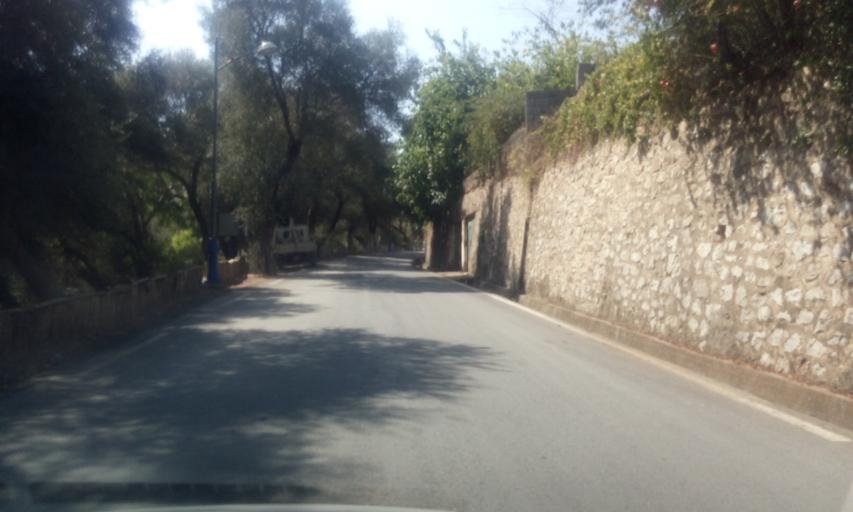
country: DZ
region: Bejaia
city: Bejaia
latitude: 36.7570
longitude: 5.0903
